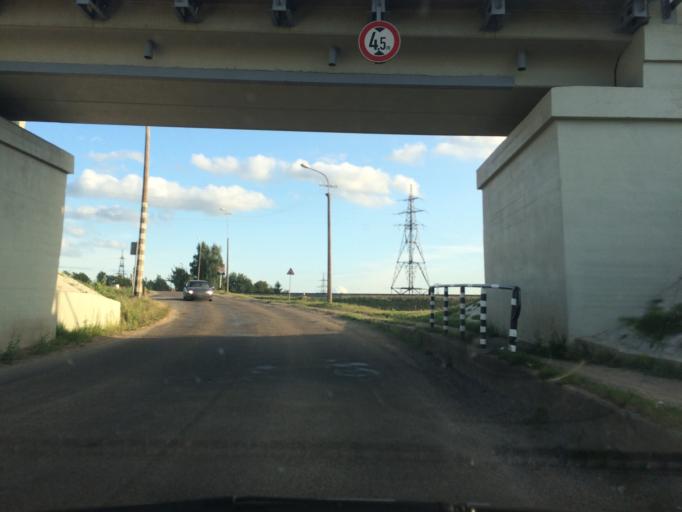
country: LV
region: Rezekne
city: Rezekne
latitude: 56.5223
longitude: 27.3189
